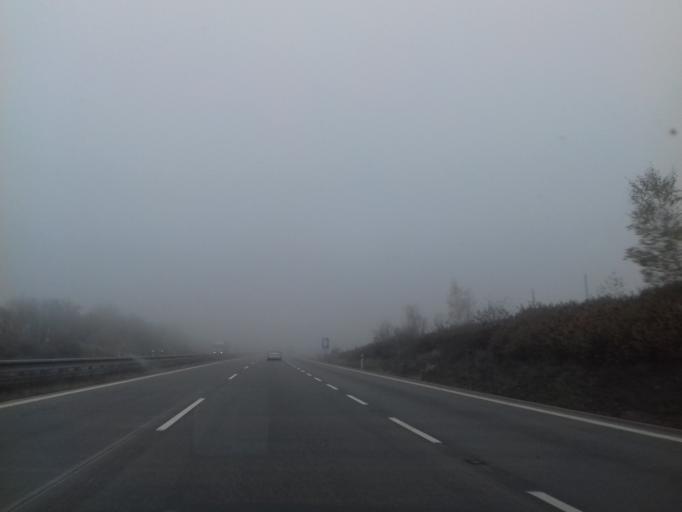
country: CZ
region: Vysocina
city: Stoky
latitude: 49.4820
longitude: 15.5359
